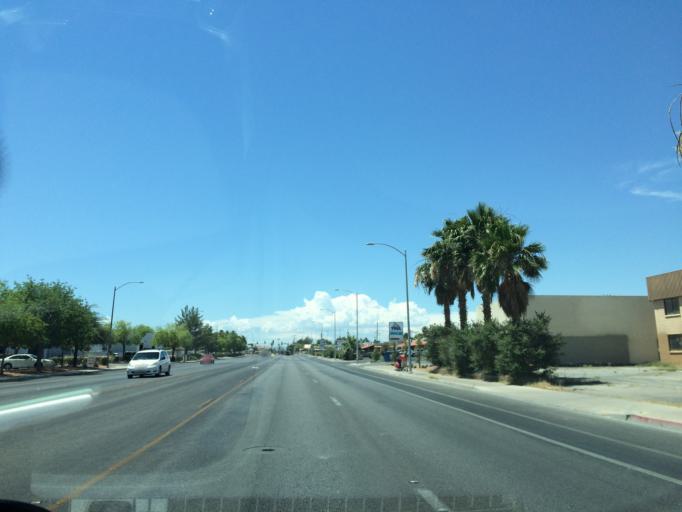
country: US
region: Nevada
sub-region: Clark County
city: Las Vegas
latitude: 36.1618
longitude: -115.1055
